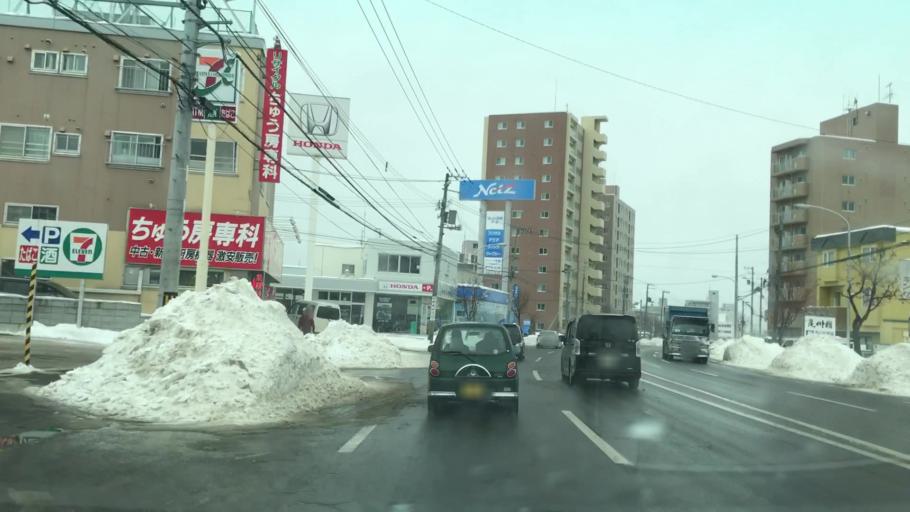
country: JP
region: Hokkaido
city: Sapporo
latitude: 43.0313
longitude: 141.3651
